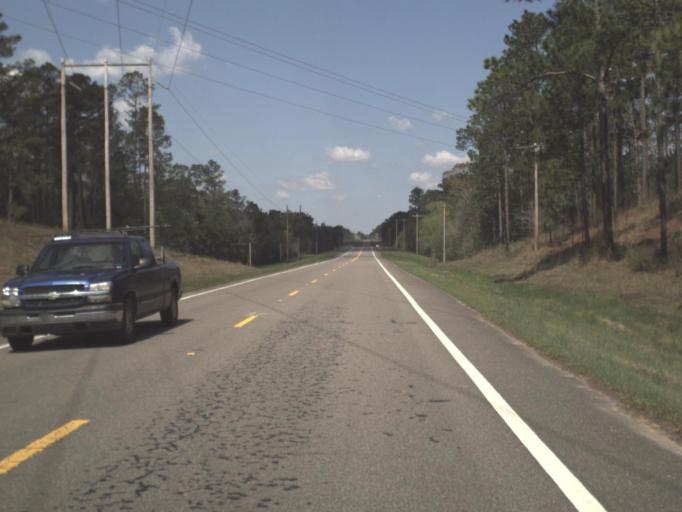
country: US
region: Florida
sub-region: Santa Rosa County
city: Point Baker
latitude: 30.8802
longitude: -86.9533
